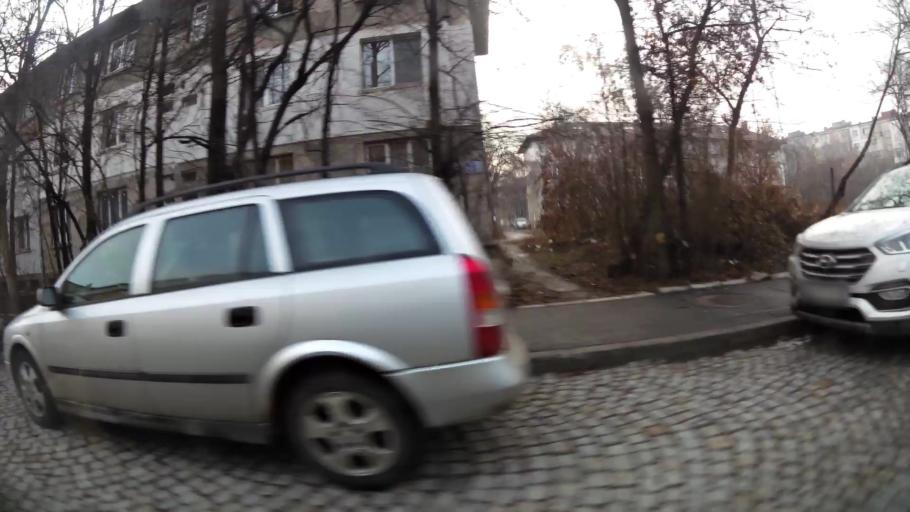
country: BG
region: Sofia-Capital
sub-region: Stolichna Obshtina
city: Sofia
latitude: 42.7309
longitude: 23.3098
